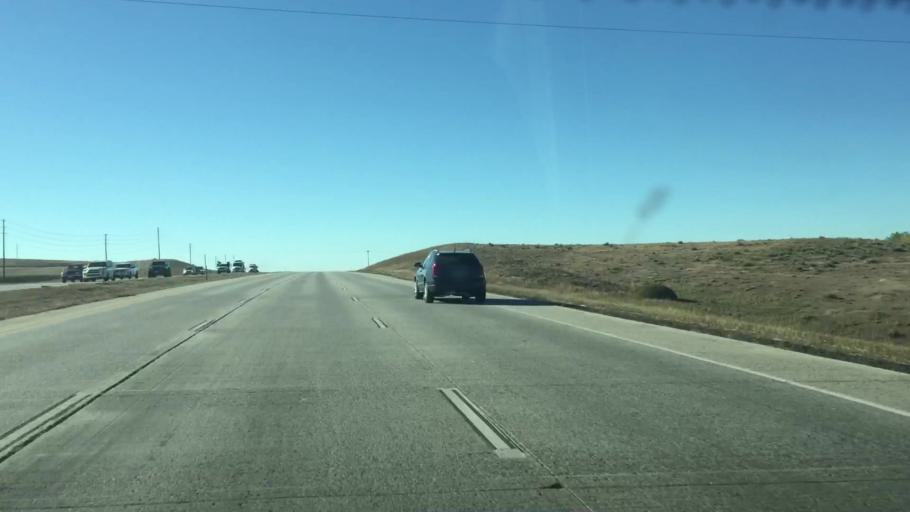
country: US
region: Colorado
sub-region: Douglas County
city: The Pinery
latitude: 39.4712
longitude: -104.7586
